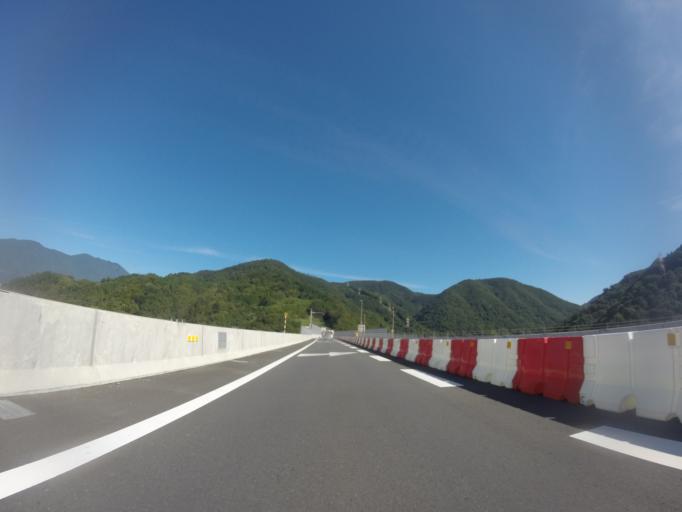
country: JP
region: Yamanashi
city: Ryuo
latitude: 35.4180
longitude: 138.4621
